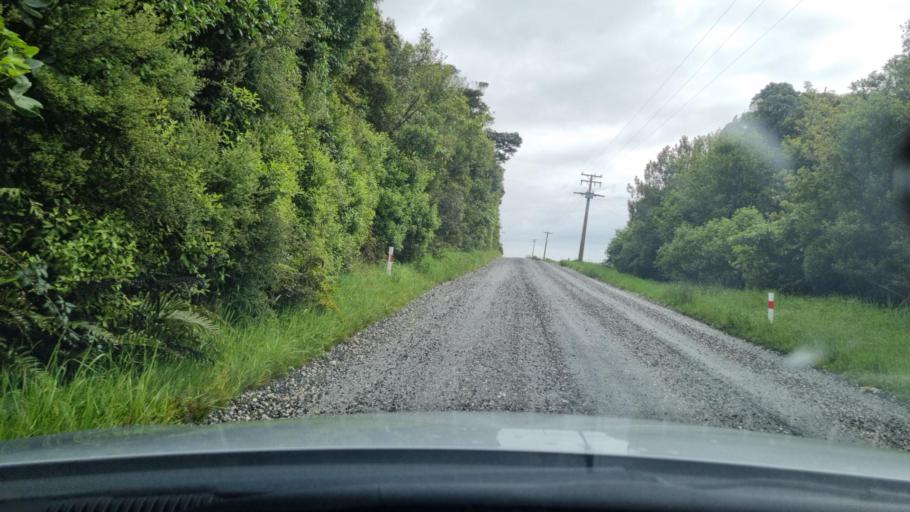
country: NZ
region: Southland
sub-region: Invercargill City
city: Bluff
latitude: -46.5279
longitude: 168.2693
